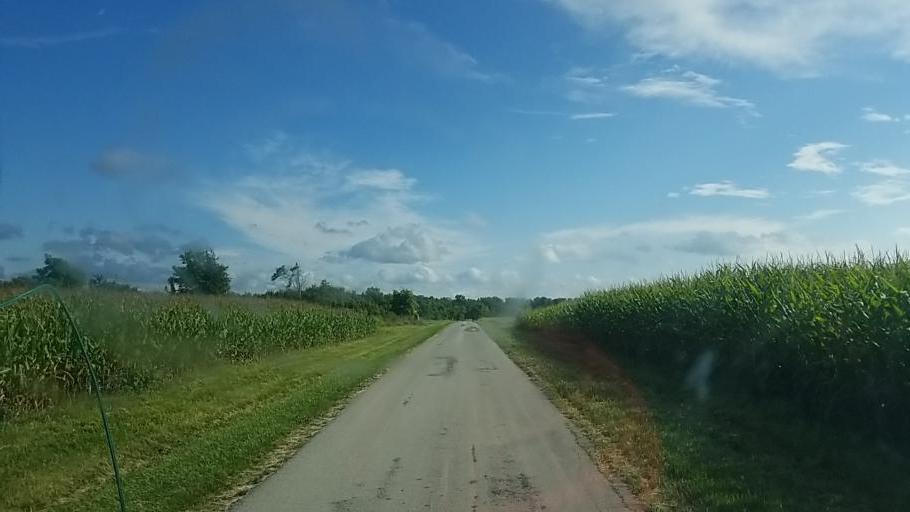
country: US
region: Ohio
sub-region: Wyandot County
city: Upper Sandusky
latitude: 40.7672
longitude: -83.3810
